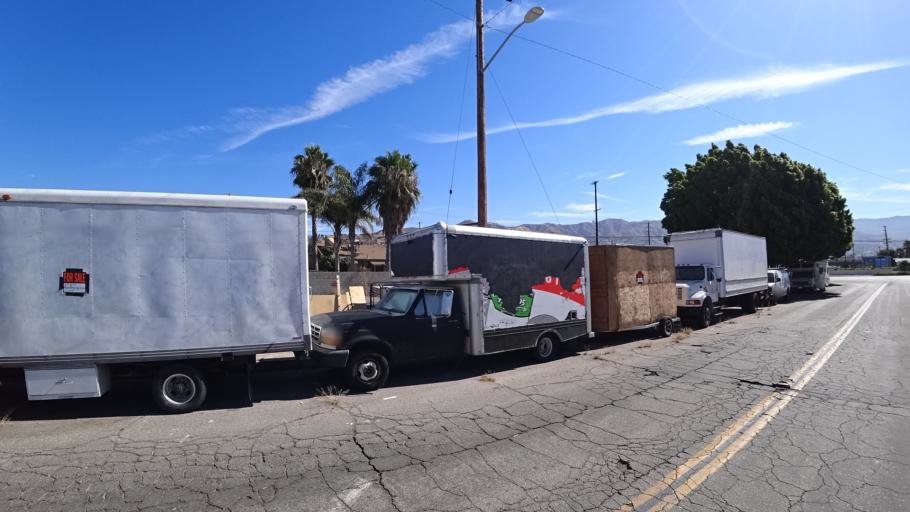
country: US
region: California
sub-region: Los Angeles County
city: North Hollywood
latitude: 34.2067
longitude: -118.3520
